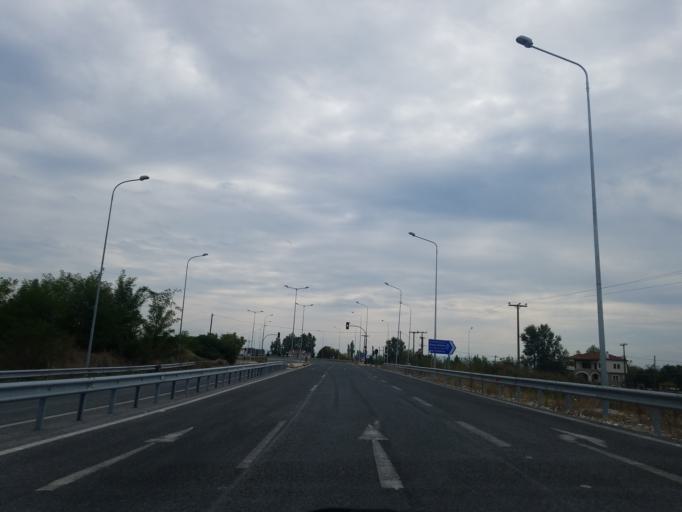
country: GR
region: Thessaly
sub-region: Nomos Kardhitsas
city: Sofades
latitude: 39.3028
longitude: 22.1278
